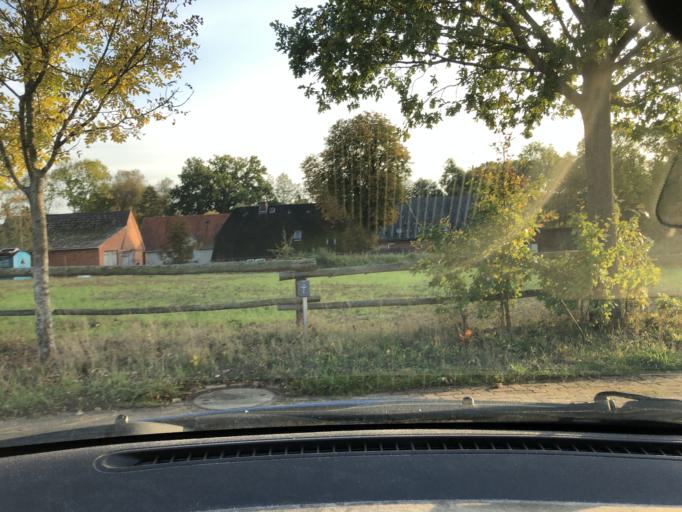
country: DE
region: Lower Saxony
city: Hitzacker
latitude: 53.1505
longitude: 11.0051
